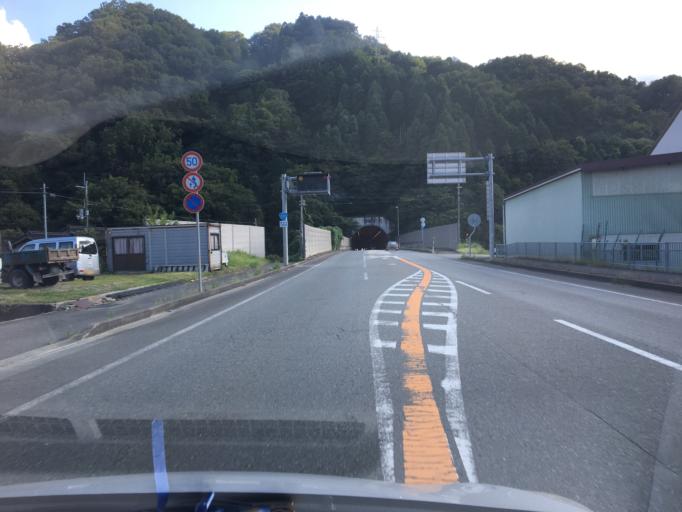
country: JP
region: Hyogo
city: Toyooka
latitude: 35.4661
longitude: 134.7683
